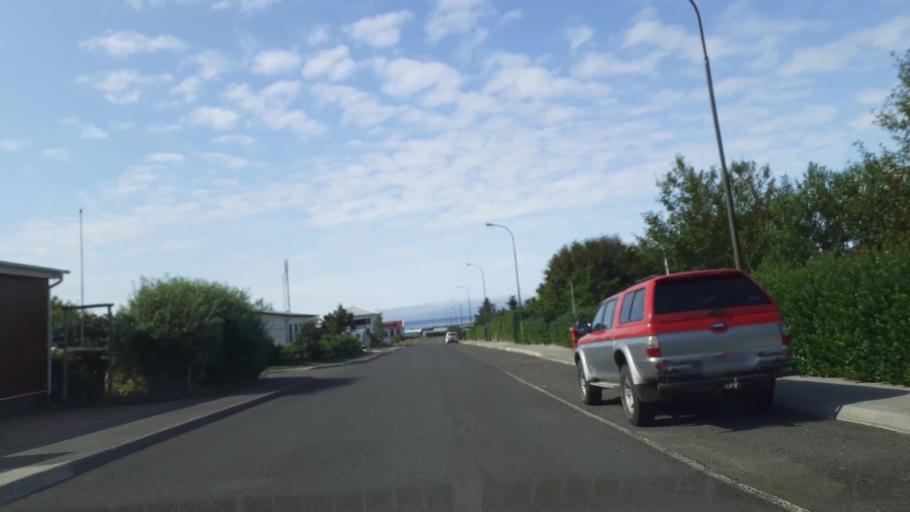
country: IS
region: Northwest
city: Saudarkrokur
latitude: 65.8249
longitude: -20.2996
